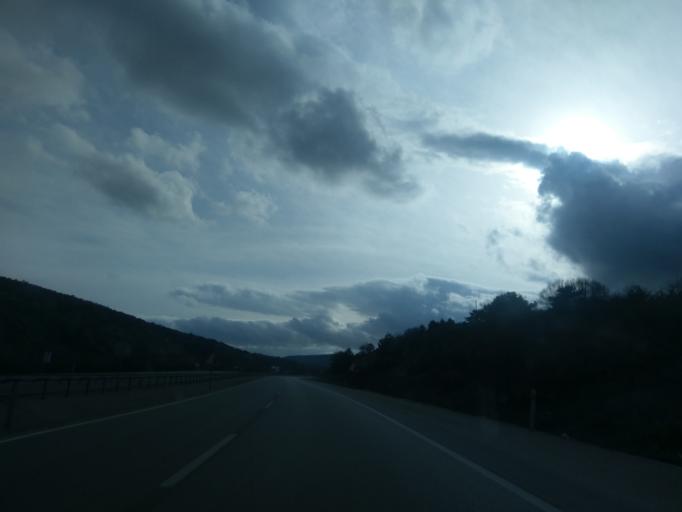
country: TR
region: Kuetahya
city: Sabuncu
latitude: 39.5527
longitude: 30.0607
